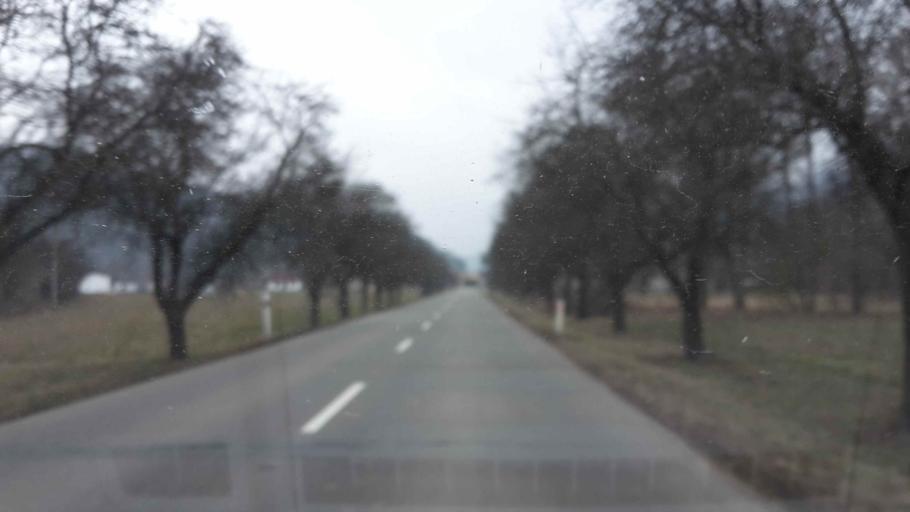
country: CZ
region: South Moravian
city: Predklasteri
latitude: 49.3673
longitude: 16.3925
